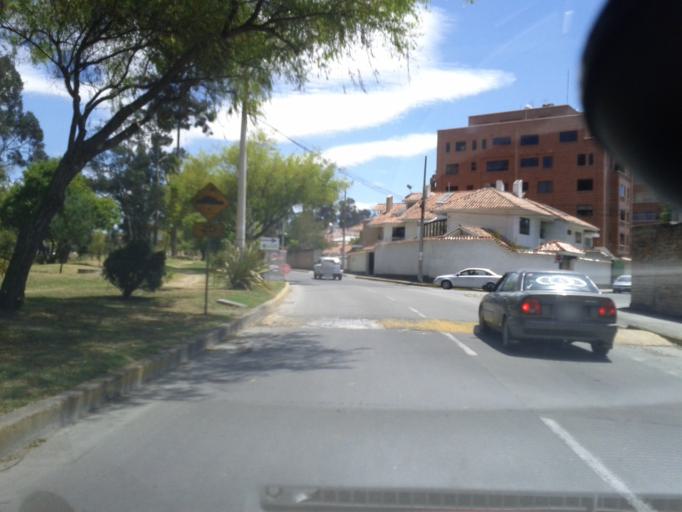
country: EC
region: Azuay
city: Cuenca
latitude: -2.8926
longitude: -79.0220
